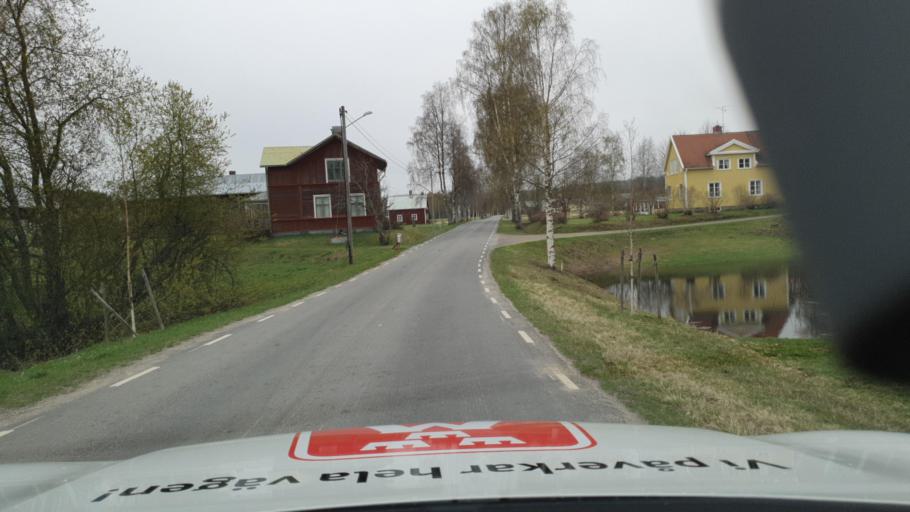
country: SE
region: Vaesterbotten
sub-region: Nordmalings Kommun
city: Nordmaling
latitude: 63.7214
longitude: 19.5217
